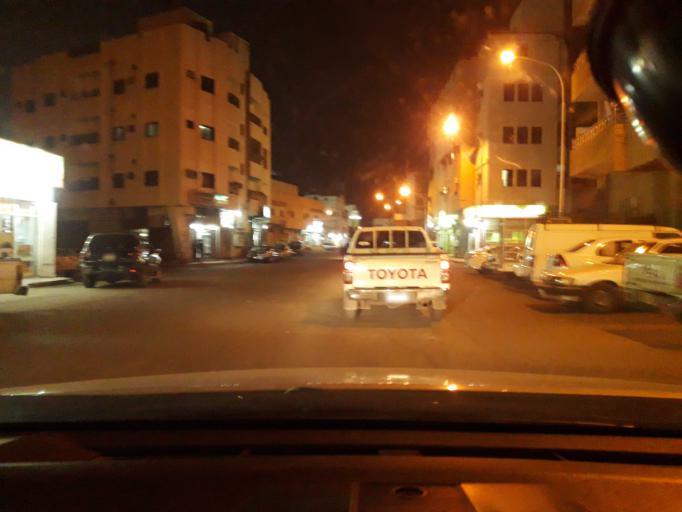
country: SA
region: Al Madinah al Munawwarah
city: Medina
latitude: 24.4655
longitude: 39.6289
